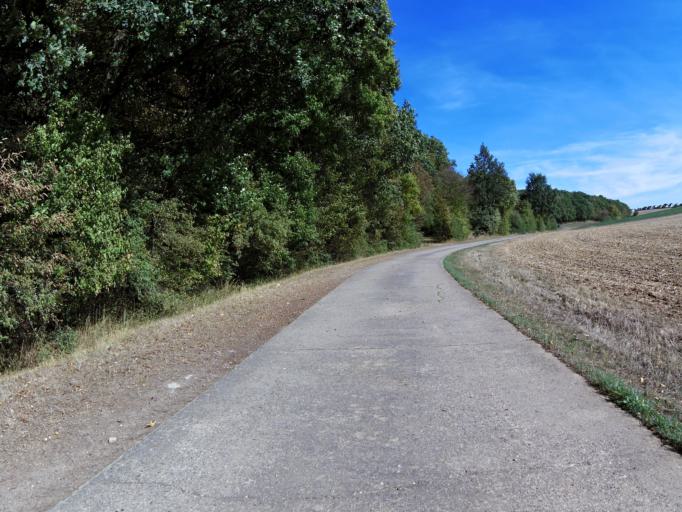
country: DE
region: Bavaria
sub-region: Regierungsbezirk Unterfranken
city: Eisingen
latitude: 49.7701
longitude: 9.8237
